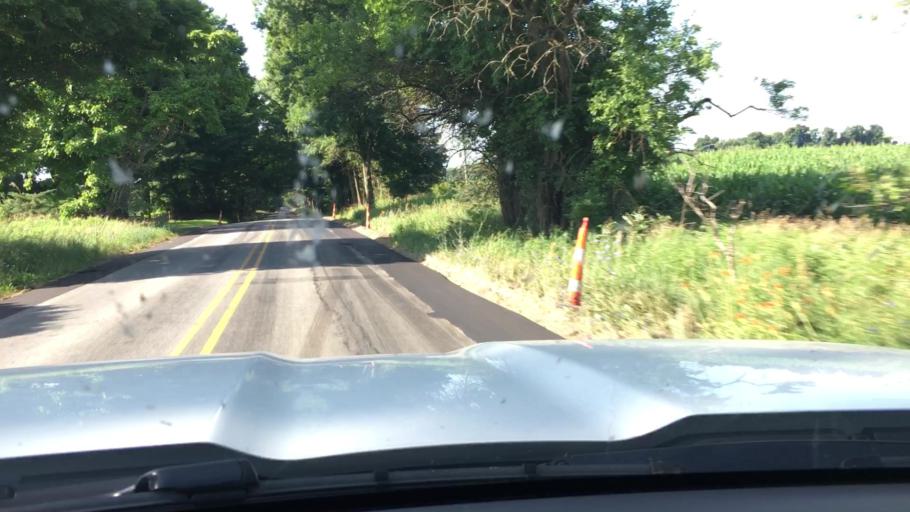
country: US
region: Michigan
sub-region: Kalamazoo County
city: South Gull Lake
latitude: 42.4198
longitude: -85.4551
